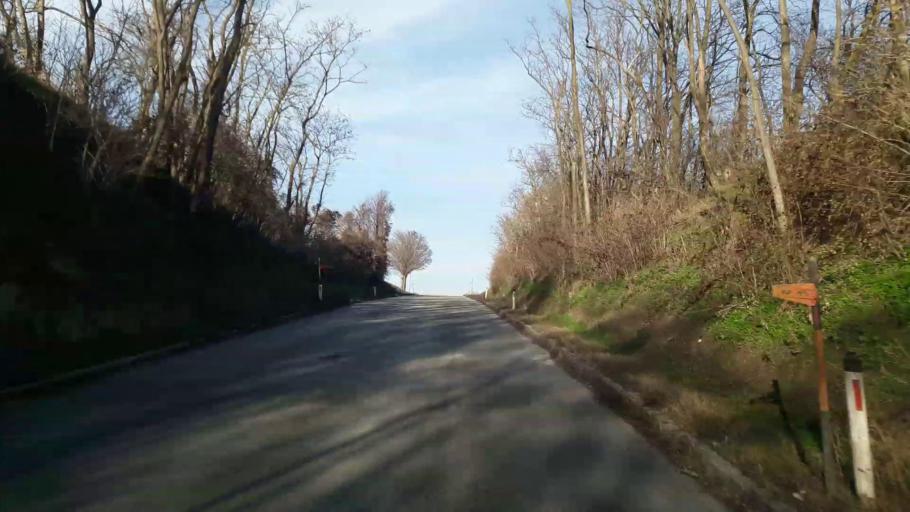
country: AT
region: Lower Austria
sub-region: Politischer Bezirk Ganserndorf
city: Gross-Schweinbarth
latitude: 48.3914
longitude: 16.6325
